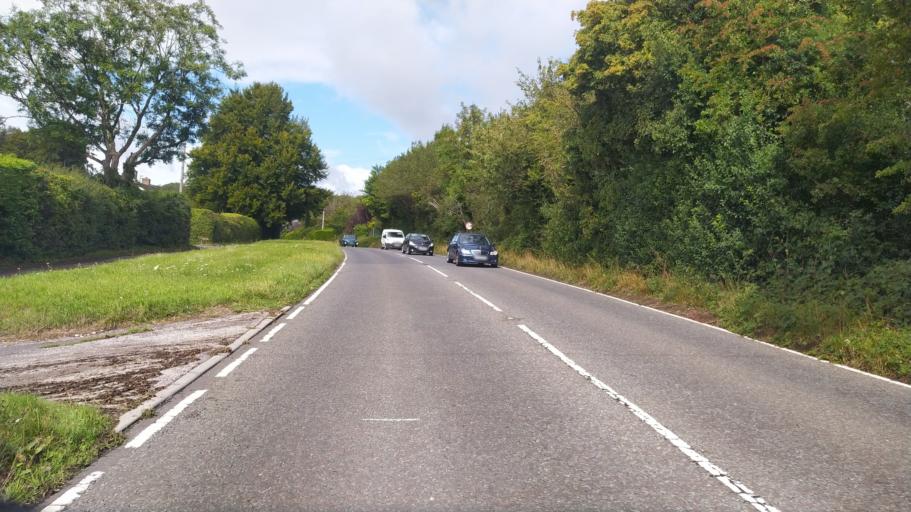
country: GB
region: England
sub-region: Dorset
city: Blandford Forum
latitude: 50.8427
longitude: -2.0999
